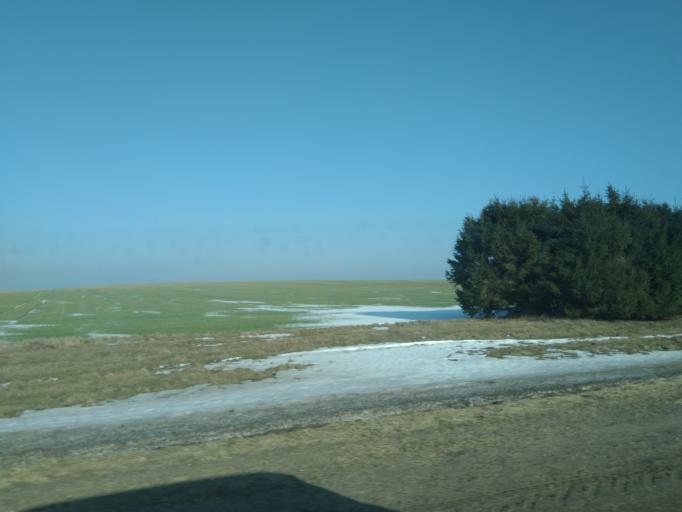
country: BY
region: Minsk
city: Snow
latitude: 53.2119
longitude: 26.4617
